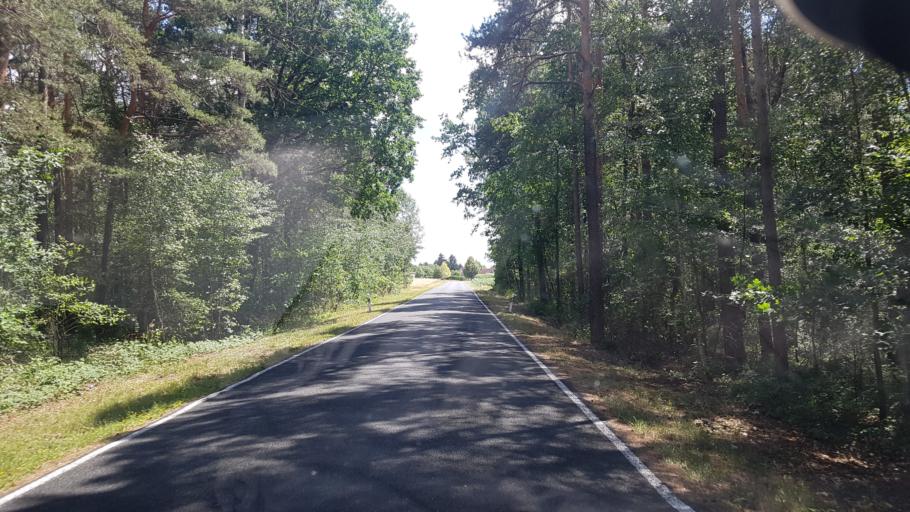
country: DE
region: Brandenburg
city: Schipkau
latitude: 51.5745
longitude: 13.9215
